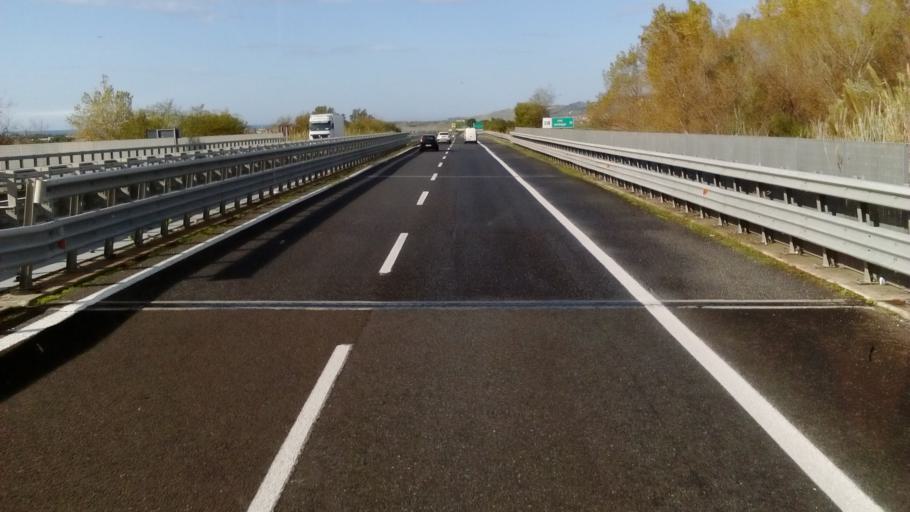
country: IT
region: Calabria
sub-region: Provincia di Catanzaro
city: Santa Eufemia Lamezia
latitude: 38.9278
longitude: 16.2441
